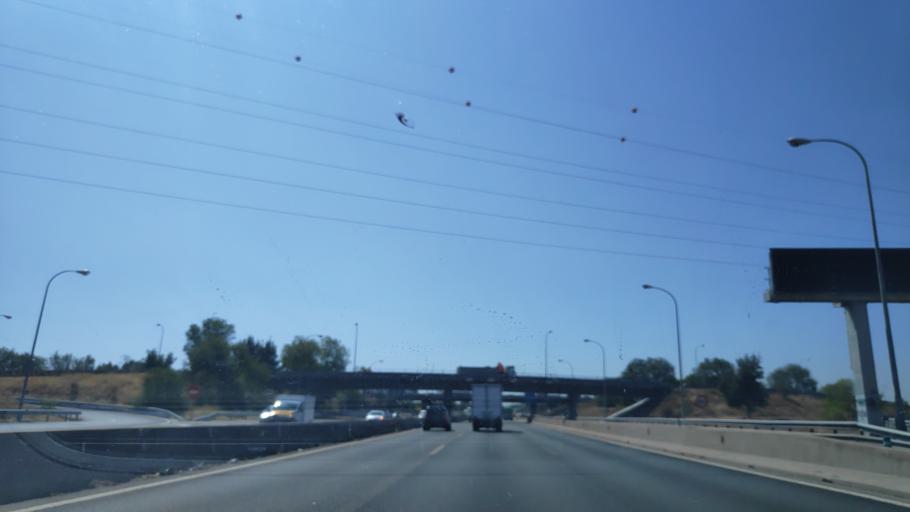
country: ES
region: Madrid
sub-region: Provincia de Madrid
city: Carabanchel
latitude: 40.3672
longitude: -3.7206
